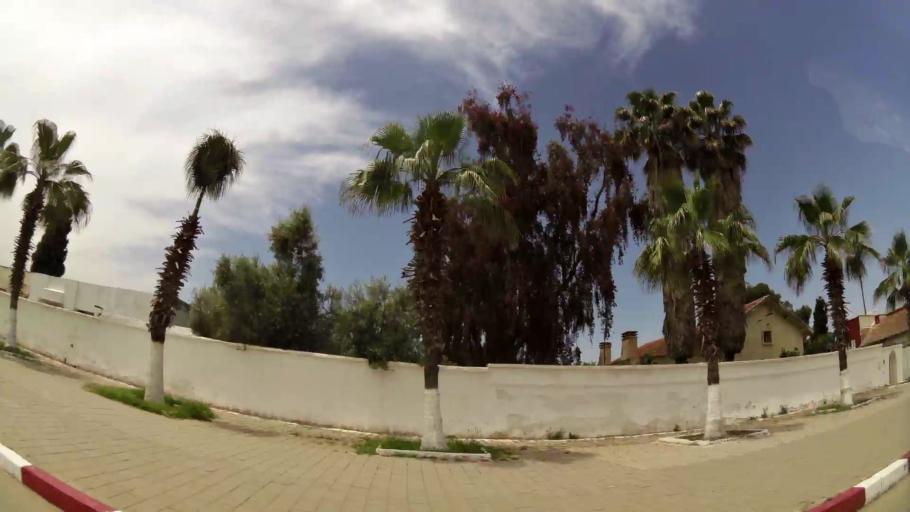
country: MA
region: Rabat-Sale-Zemmour-Zaer
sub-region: Khemisset
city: Khemisset
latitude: 33.8205
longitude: -6.0678
